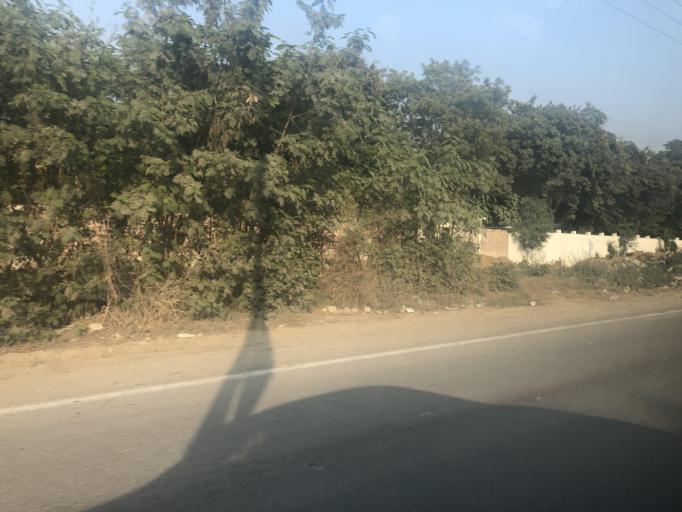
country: IN
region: Haryana
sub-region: Gurgaon
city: Gurgaon
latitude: 28.5388
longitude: 77.0321
